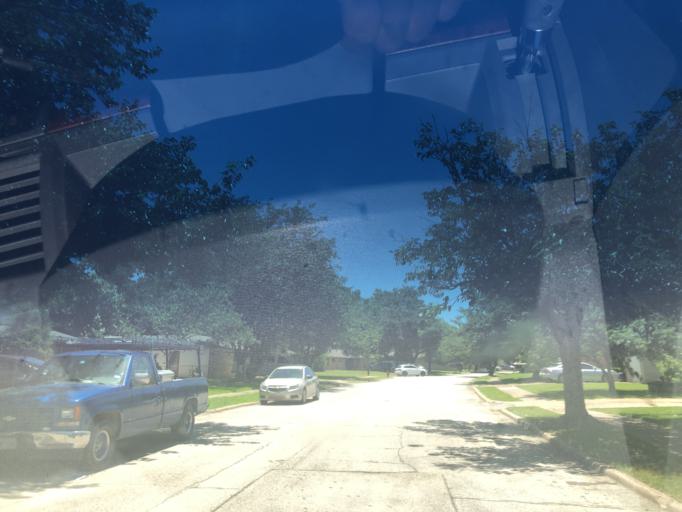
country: US
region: Texas
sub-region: Dallas County
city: Grand Prairie
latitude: 32.7183
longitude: -97.0095
